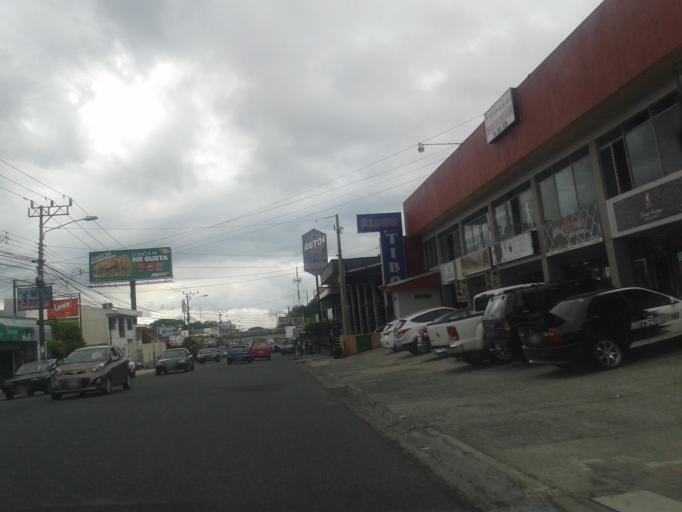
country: CR
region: San Jose
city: San Juan
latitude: 9.9621
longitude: -84.0702
